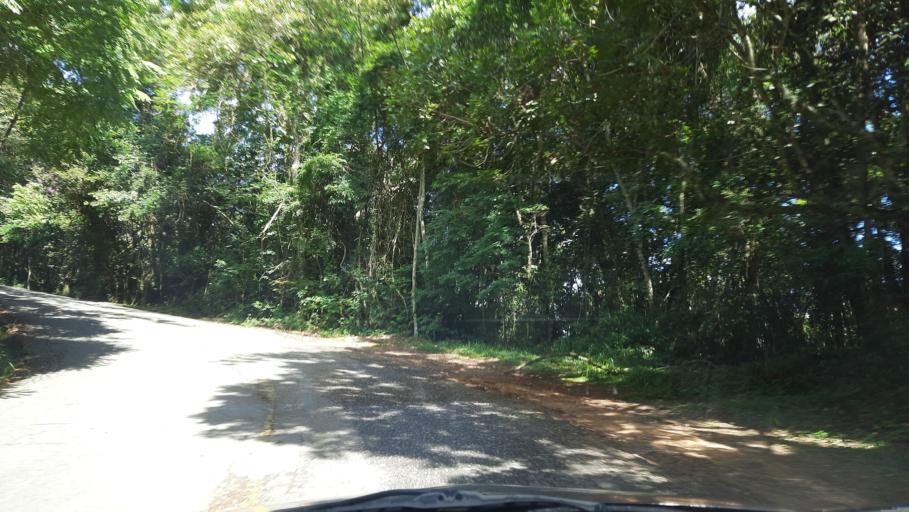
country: BR
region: Minas Gerais
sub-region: Pocos De Caldas
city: Pocos de Caldas
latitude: -21.7776
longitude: -46.5624
